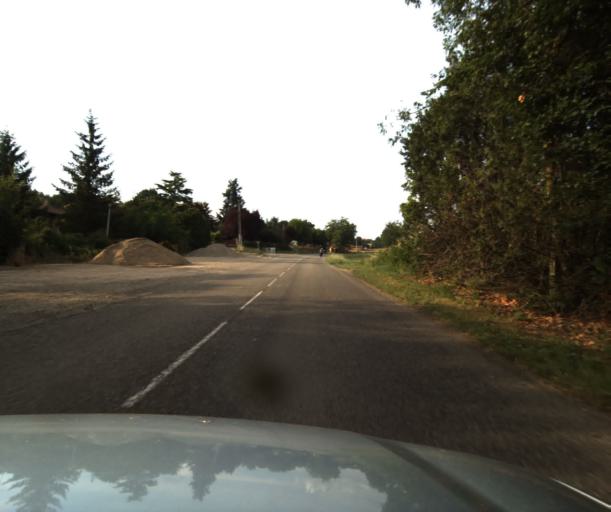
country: FR
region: Midi-Pyrenees
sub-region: Departement du Tarn-et-Garonne
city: Castelsarrasin
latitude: 43.9335
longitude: 1.0866
